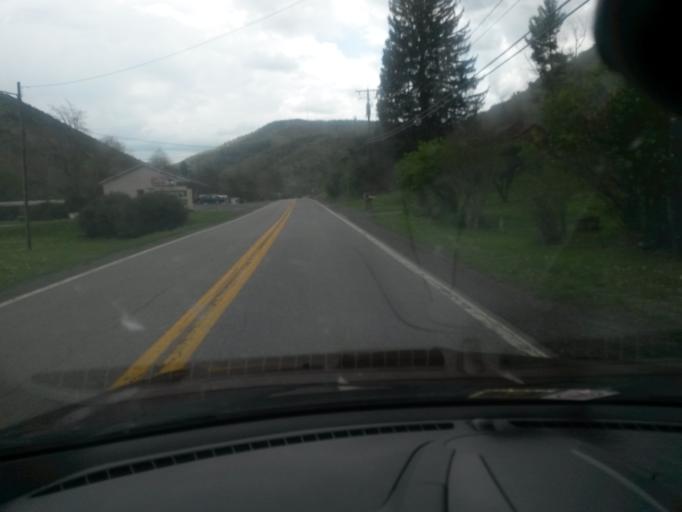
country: US
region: West Virginia
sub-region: Greenbrier County
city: White Sulphur Springs
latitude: 37.7964
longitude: -80.2775
